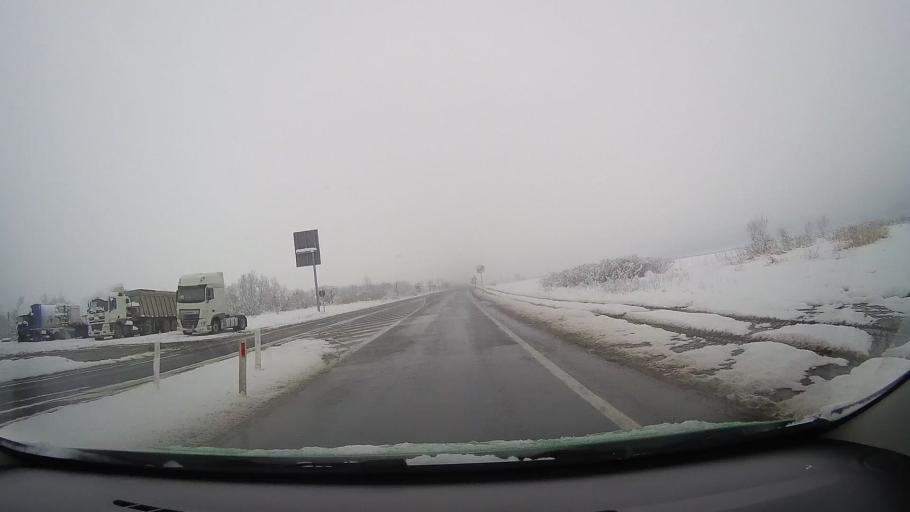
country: RO
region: Sibiu
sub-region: Oras Saliste
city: Saliste
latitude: 45.7998
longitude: 23.9016
